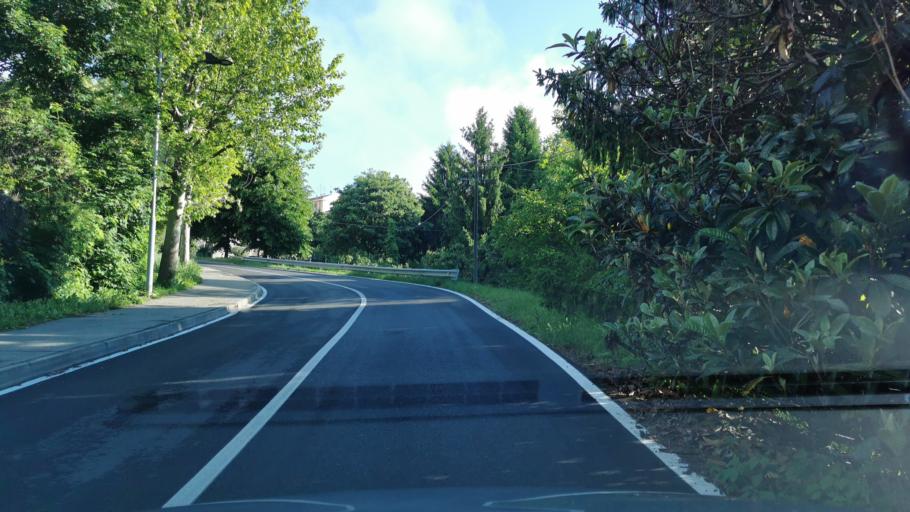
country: IT
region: Piedmont
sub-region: Provincia di Torino
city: Pino Torinese
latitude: 45.0421
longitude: 7.7730
